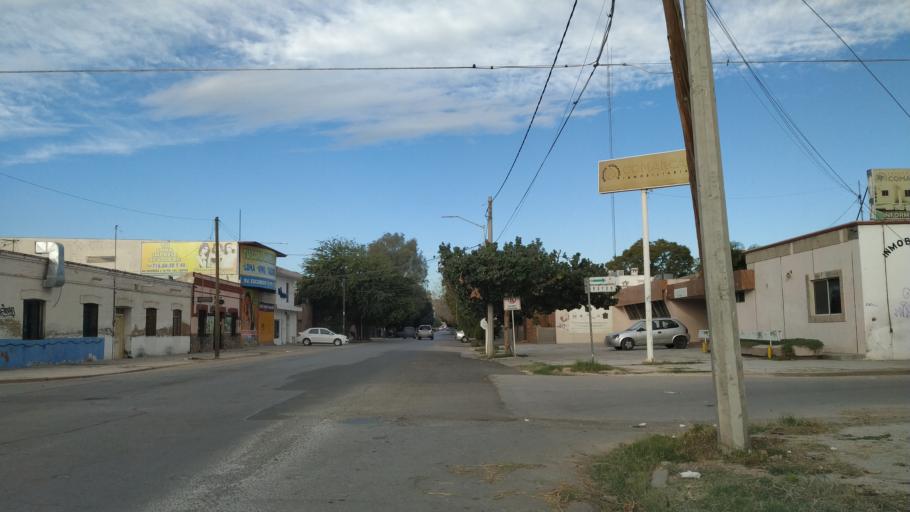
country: MX
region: Coahuila
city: Torreon
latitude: 25.5442
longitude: -103.4495
